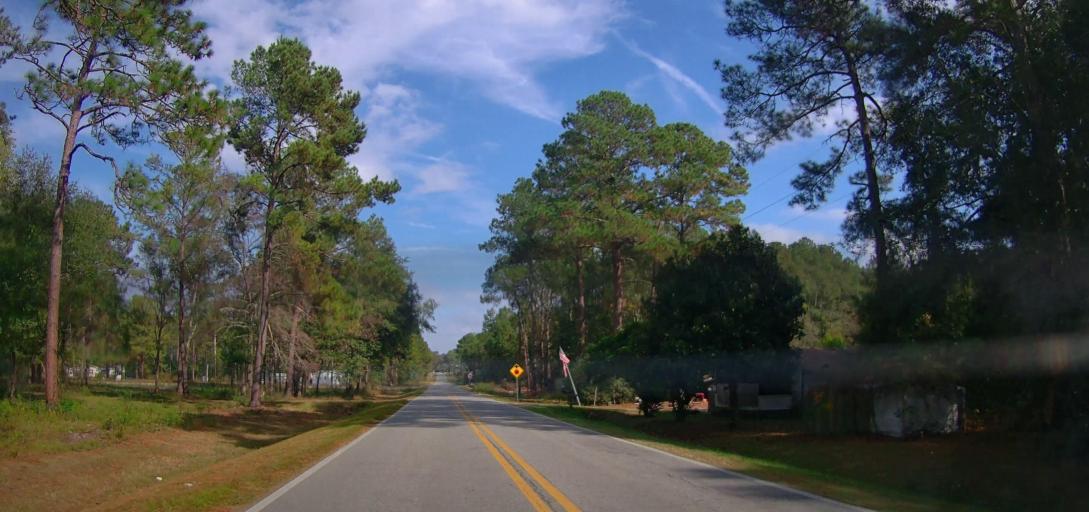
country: US
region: Georgia
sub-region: Thomas County
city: Thomasville
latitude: 30.9497
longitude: -84.0311
